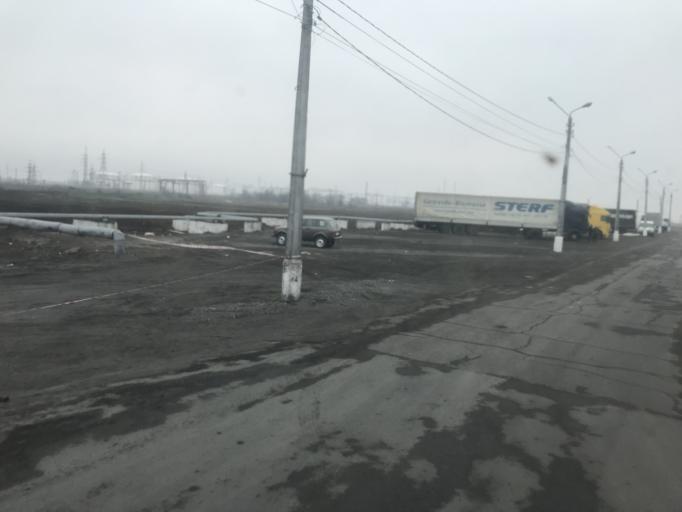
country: RU
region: Volgograd
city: Svetlyy Yar
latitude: 48.4896
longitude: 44.6631
